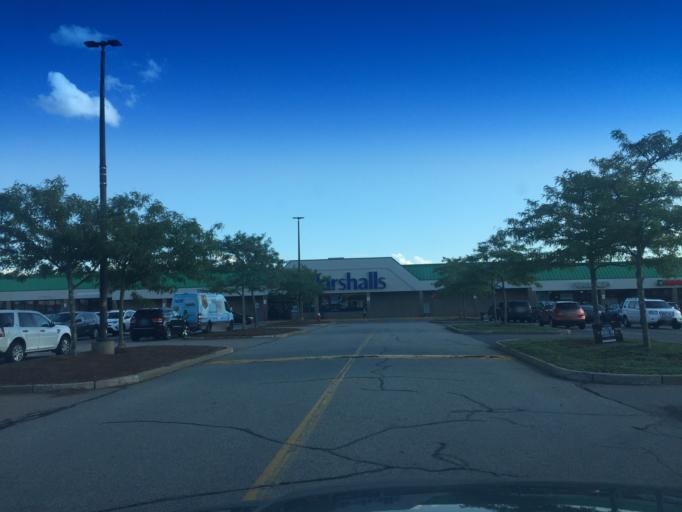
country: US
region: Massachusetts
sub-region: Norfolk County
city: Franklin
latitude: 42.0888
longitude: -71.4232
